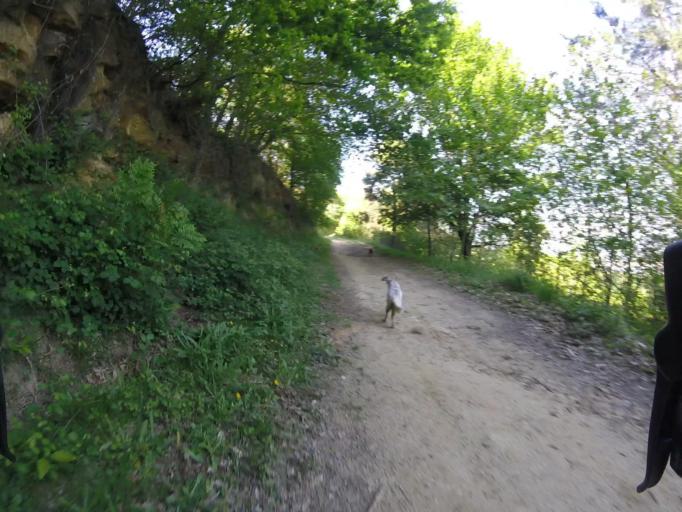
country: ES
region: Basque Country
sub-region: Provincia de Guipuzcoa
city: Fuenterrabia
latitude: 43.3646
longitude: -1.8234
